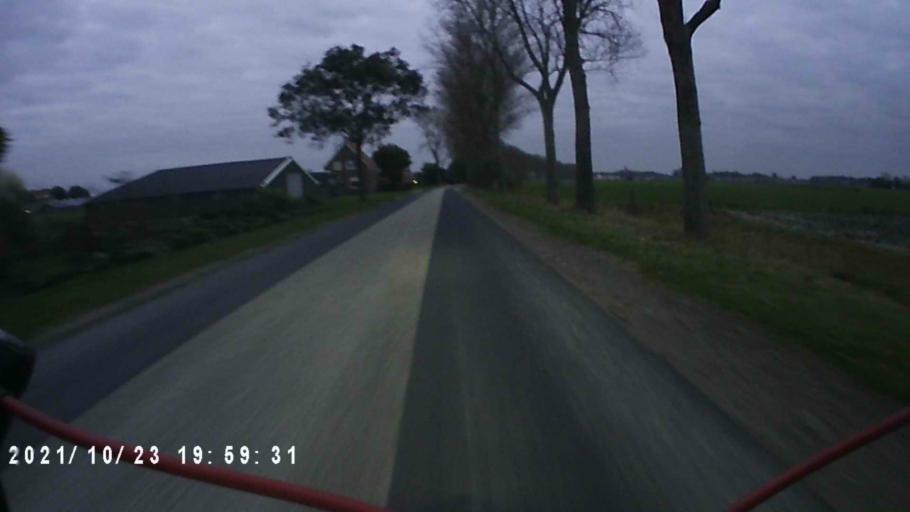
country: NL
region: Friesland
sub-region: Gemeente Harlingen
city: Harlingen
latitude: 53.1107
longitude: 5.4574
